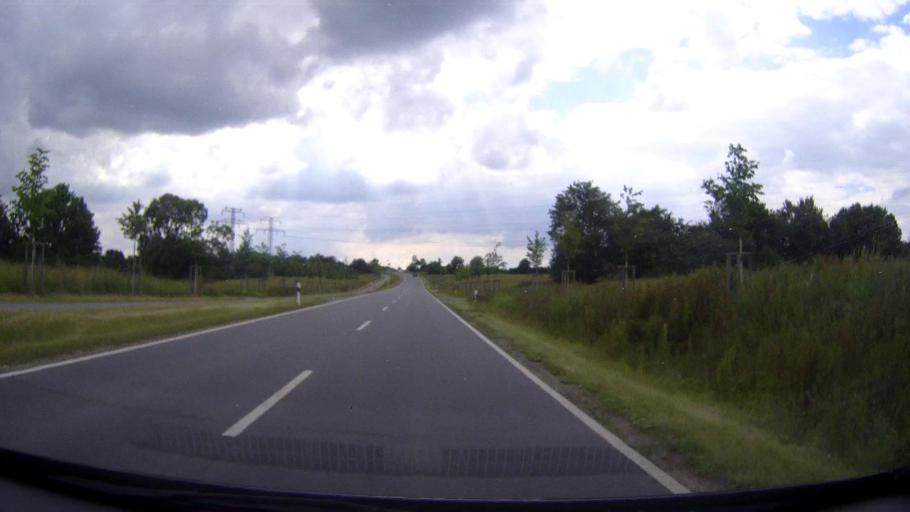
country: DE
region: Schleswig-Holstein
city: Stockelsdorf
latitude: 53.8891
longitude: 10.6150
